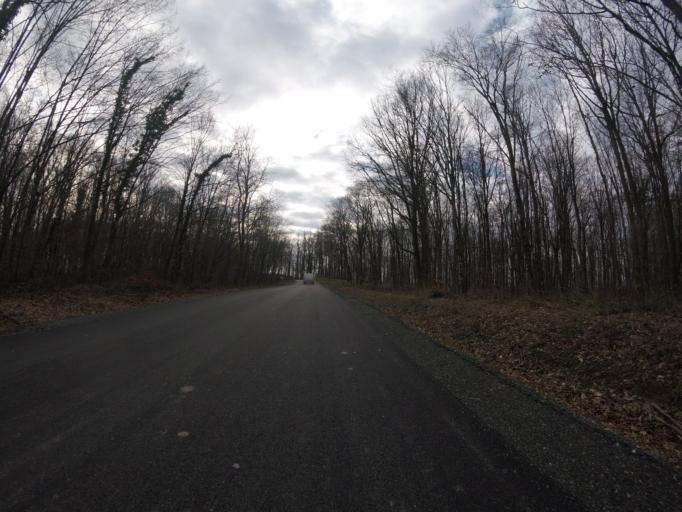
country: HR
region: Sisacko-Moslavacka
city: Glina
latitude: 45.4901
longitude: 16.0451
